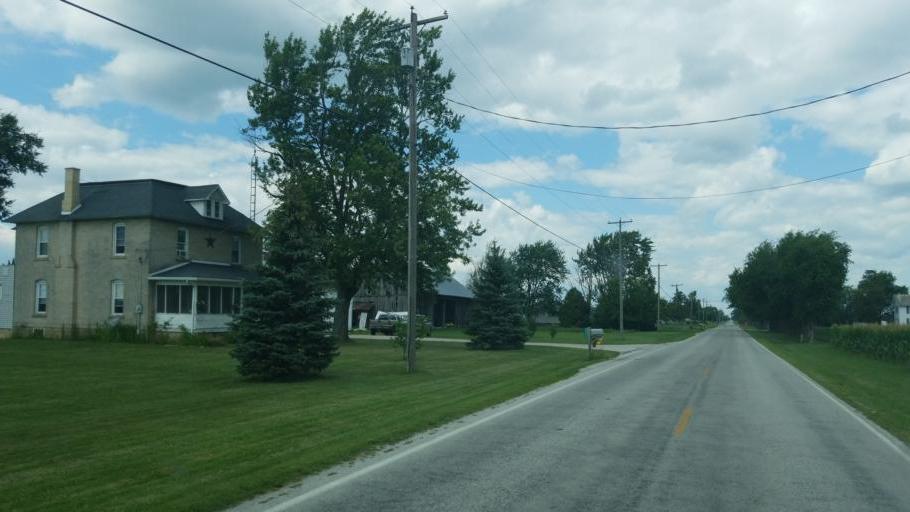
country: US
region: Ohio
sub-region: Ottawa County
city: Genoa
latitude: 41.5722
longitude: -83.2804
